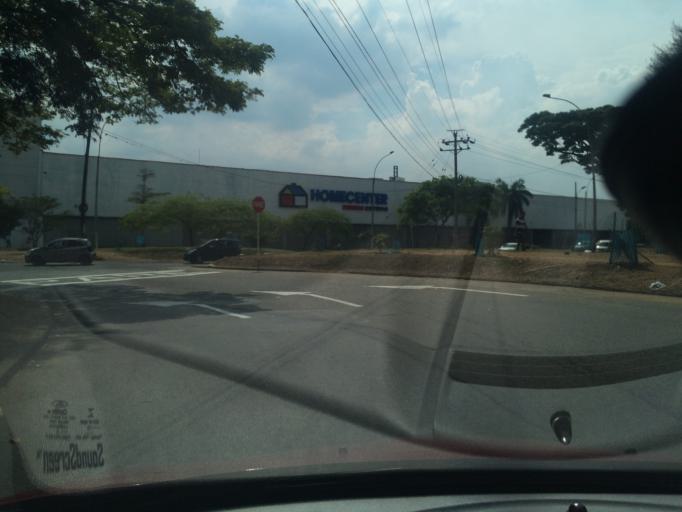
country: CO
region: Valle del Cauca
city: Cali
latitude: 3.3673
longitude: -76.5253
